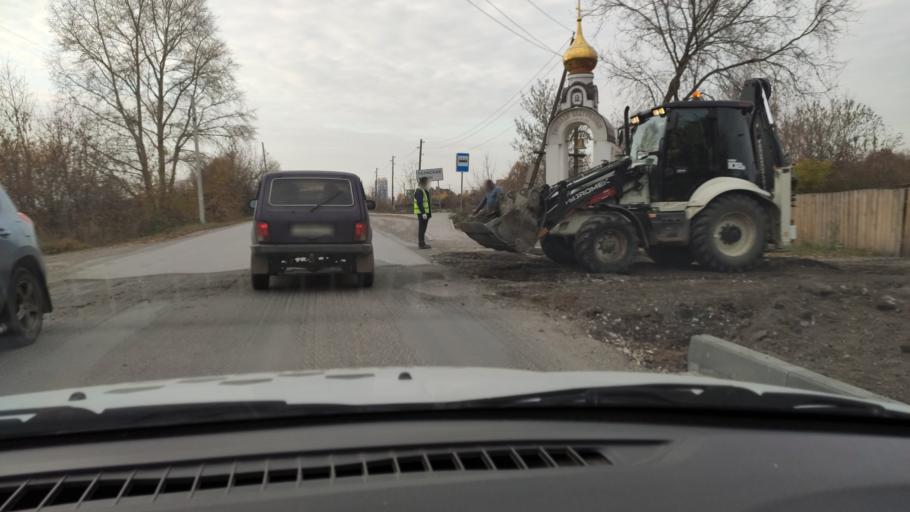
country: RU
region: Perm
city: Kondratovo
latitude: 57.9668
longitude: 56.1184
